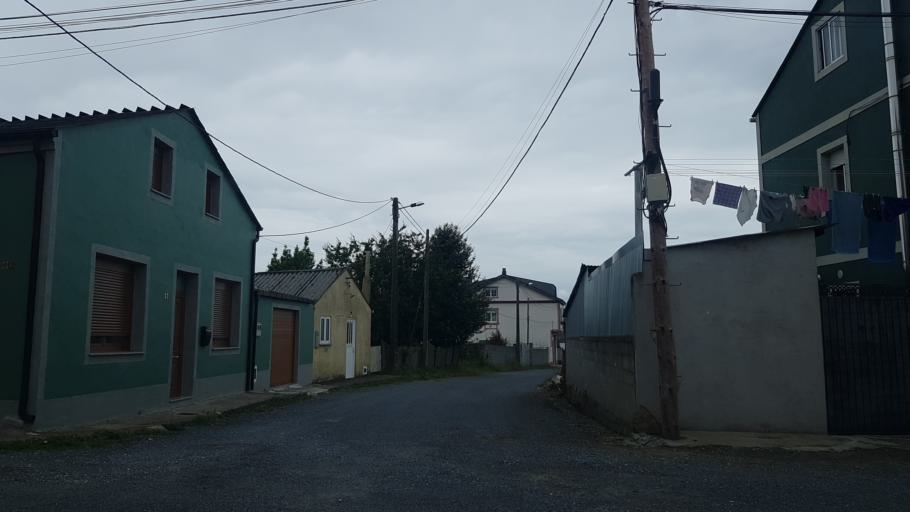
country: ES
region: Galicia
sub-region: Provincia de Lugo
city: Lugo
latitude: 43.0259
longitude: -7.5486
